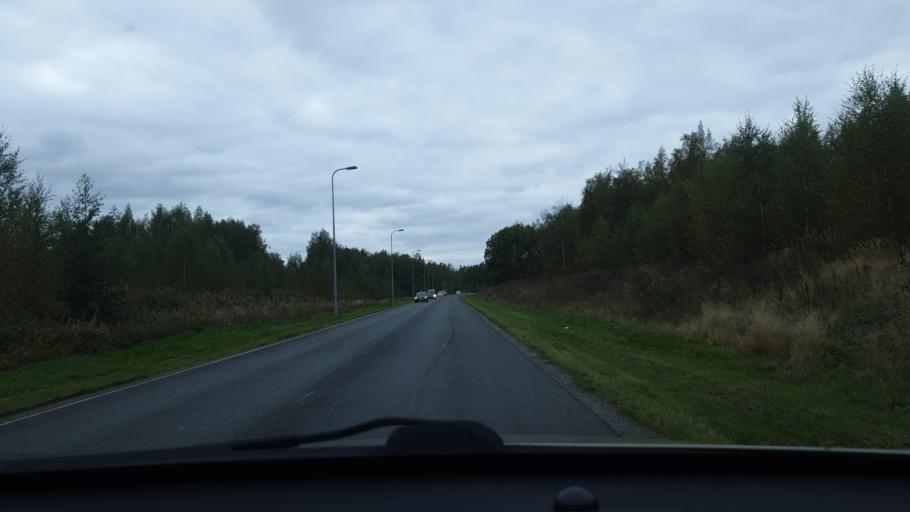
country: FI
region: Ostrobothnia
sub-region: Vaasa
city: Teeriniemi
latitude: 63.1016
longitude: 21.6905
